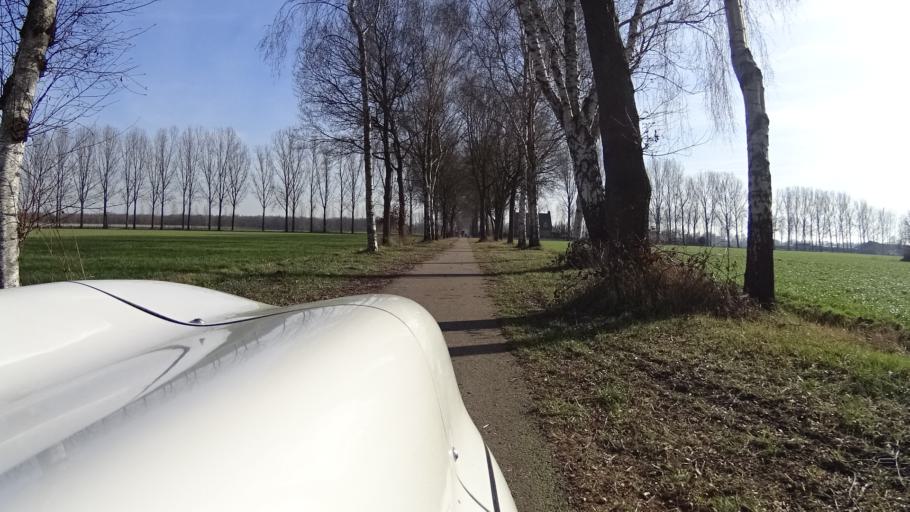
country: NL
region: North Brabant
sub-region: Gemeente Veghel
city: Mariaheide
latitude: 51.6194
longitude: 5.5680
